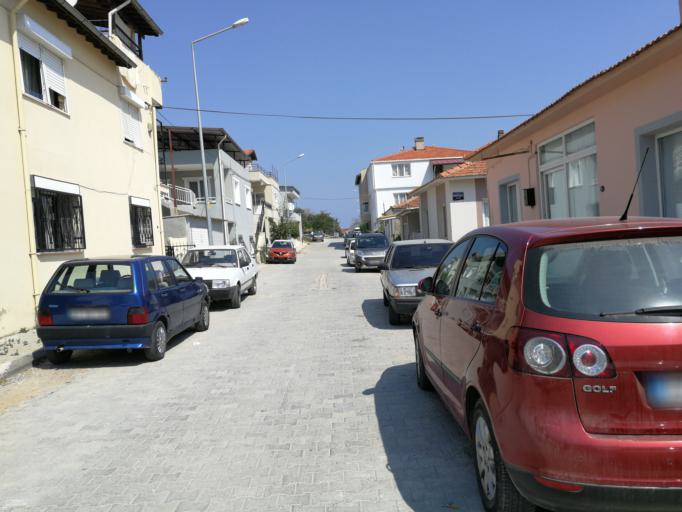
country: TR
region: Izmir
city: Urla
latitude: 38.3229
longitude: 26.7711
